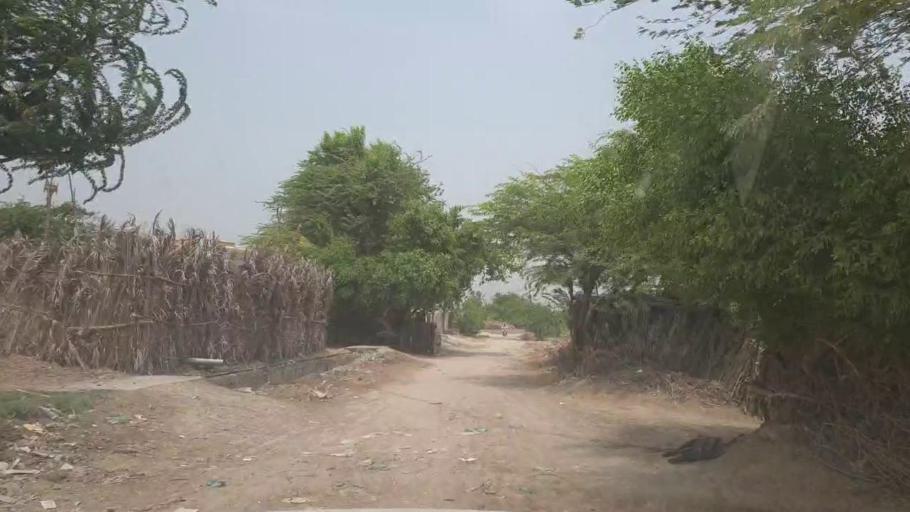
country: PK
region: Sindh
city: Kot Diji
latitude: 27.4372
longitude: 68.6446
